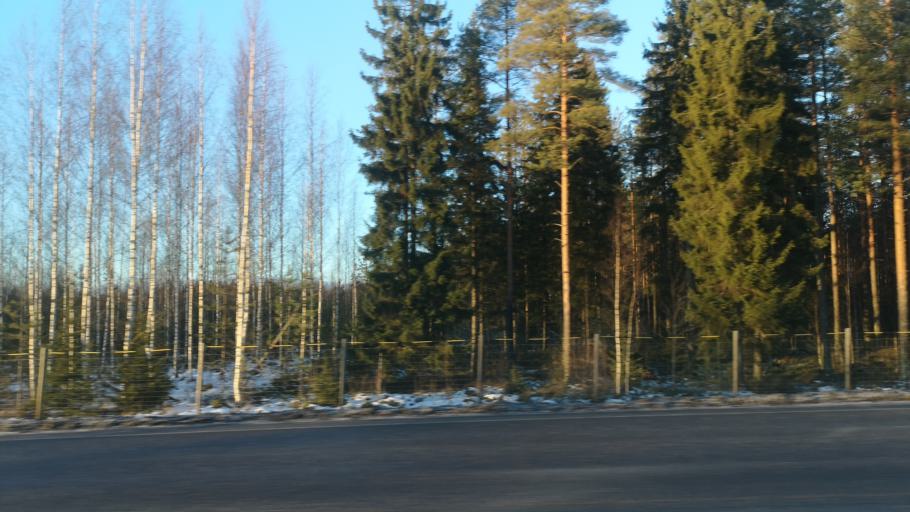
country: FI
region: Southern Savonia
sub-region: Pieksaemaeki
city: Juva
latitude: 61.8696
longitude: 27.7460
